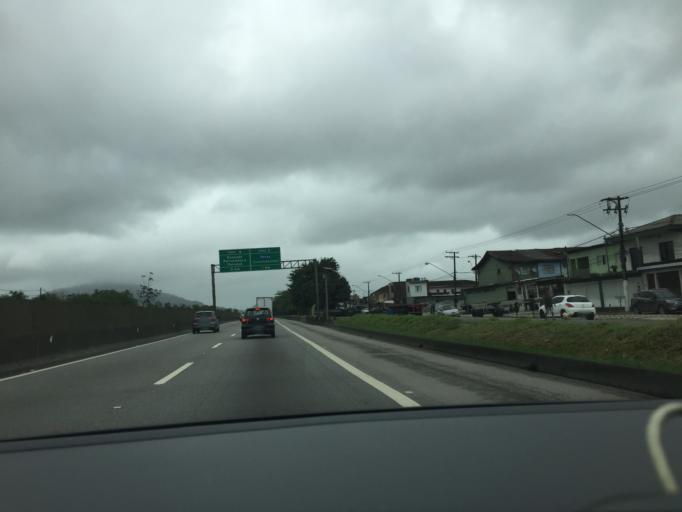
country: BR
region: Sao Paulo
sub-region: Guaruja
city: Guaruja
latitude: -23.9511
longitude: -46.2770
